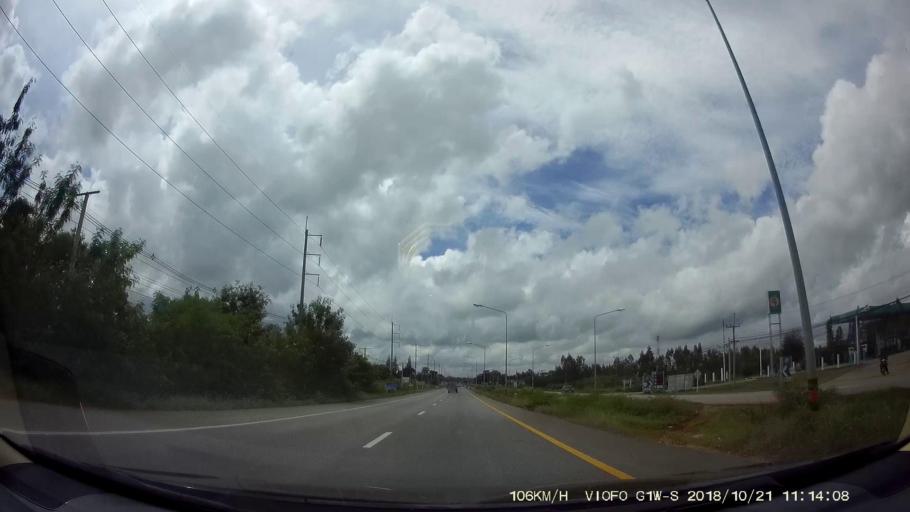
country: TH
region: Chaiyaphum
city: Chaiyaphum
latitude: 15.9077
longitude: 102.1254
